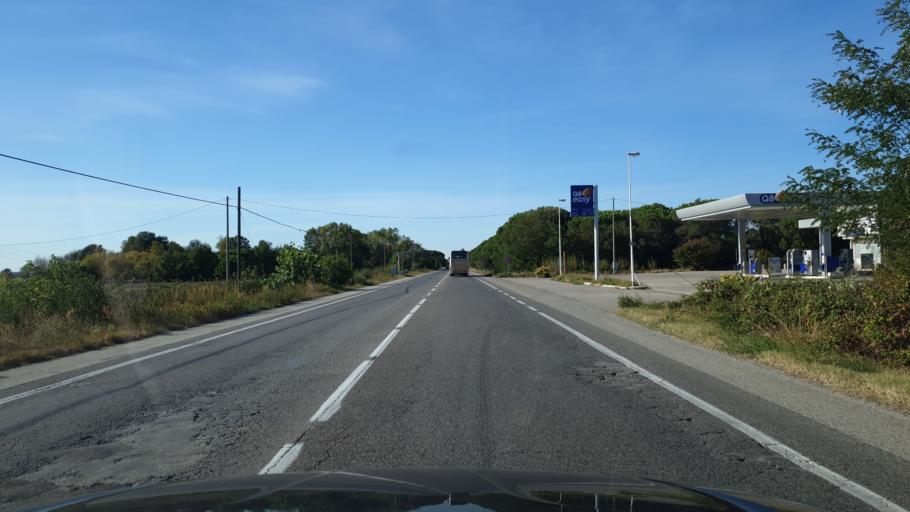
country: IT
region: Emilia-Romagna
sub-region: Provincia di Ravenna
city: Cervia
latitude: 44.2745
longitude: 12.3233
